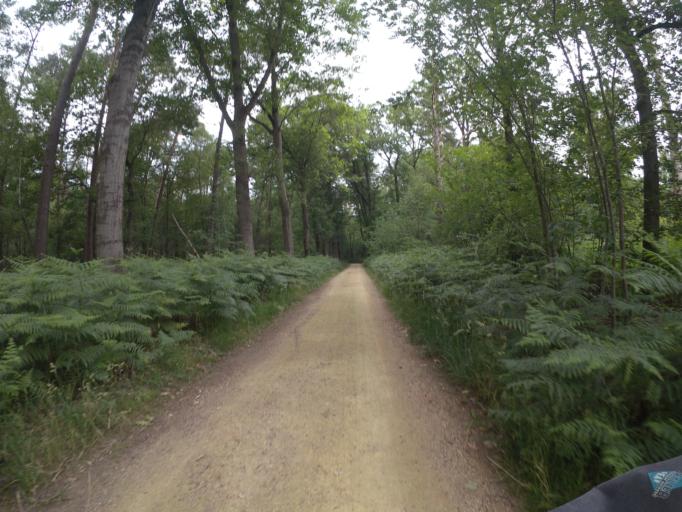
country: NL
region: North Brabant
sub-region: Gemeente Best
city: Best
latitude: 51.5376
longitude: 5.3568
